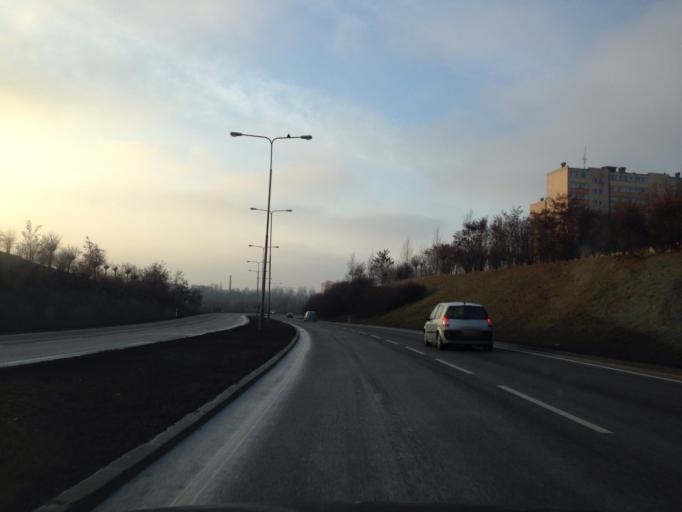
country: PL
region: Greater Poland Voivodeship
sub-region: Powiat gnieznienski
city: Gniezno
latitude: 52.5506
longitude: 17.6140
